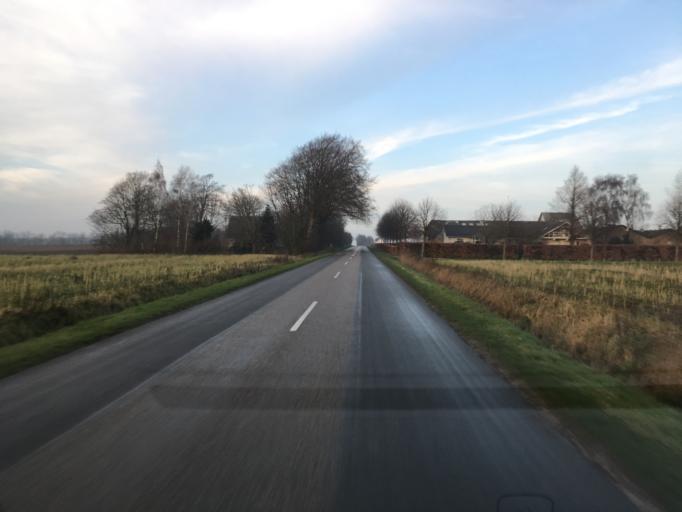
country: DK
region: South Denmark
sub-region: Tonder Kommune
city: Toftlund
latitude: 55.1301
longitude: 9.0623
